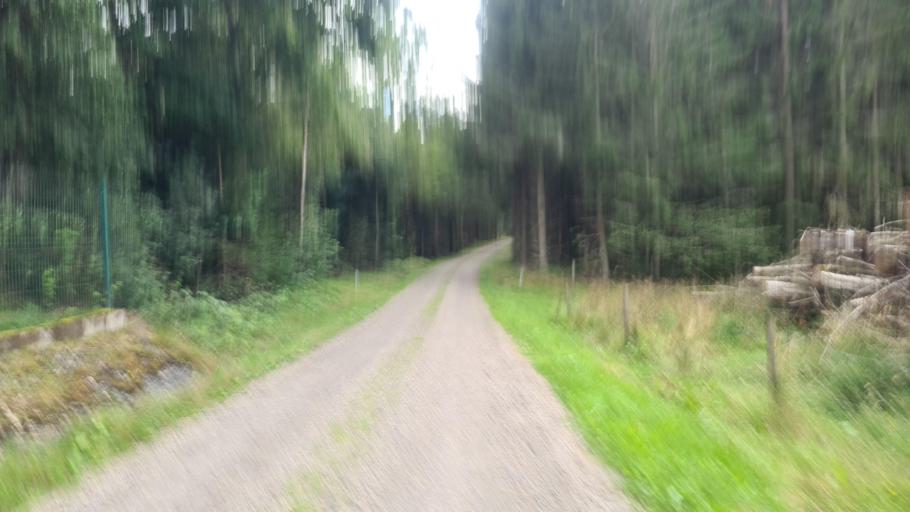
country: SE
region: Kronoberg
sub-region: Ljungby Kommun
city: Ljungby
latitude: 56.8205
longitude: 13.8632
